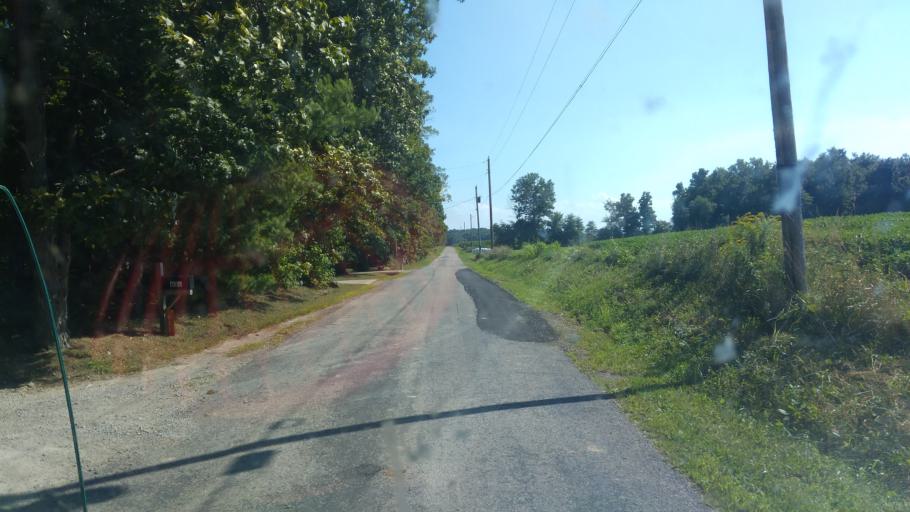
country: US
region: Ohio
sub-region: Ashland County
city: Ashland
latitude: 40.9686
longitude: -82.3301
